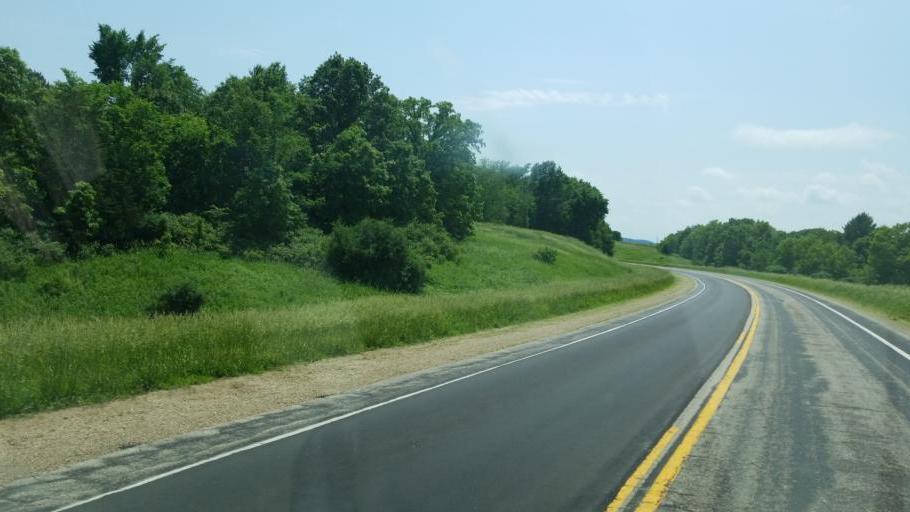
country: US
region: Wisconsin
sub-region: Monroe County
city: Cashton
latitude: 43.6040
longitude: -90.6248
